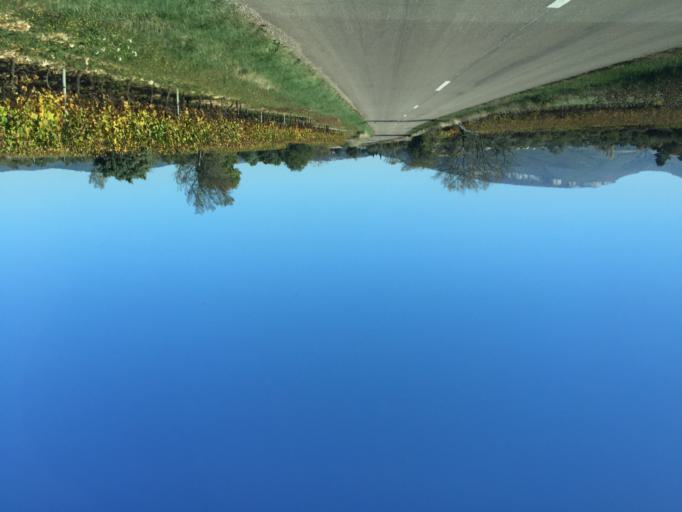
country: FR
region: Rhone-Alpes
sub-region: Departement de l'Ardeche
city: Bourg-Saint-Andeol
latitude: 44.4323
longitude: 4.5608
